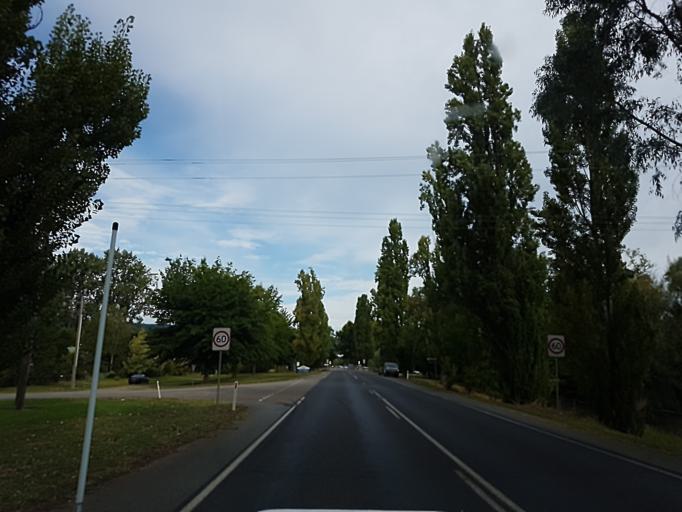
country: AU
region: Victoria
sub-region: Wangaratta
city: Wangaratta
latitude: -36.5526
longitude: 146.7106
